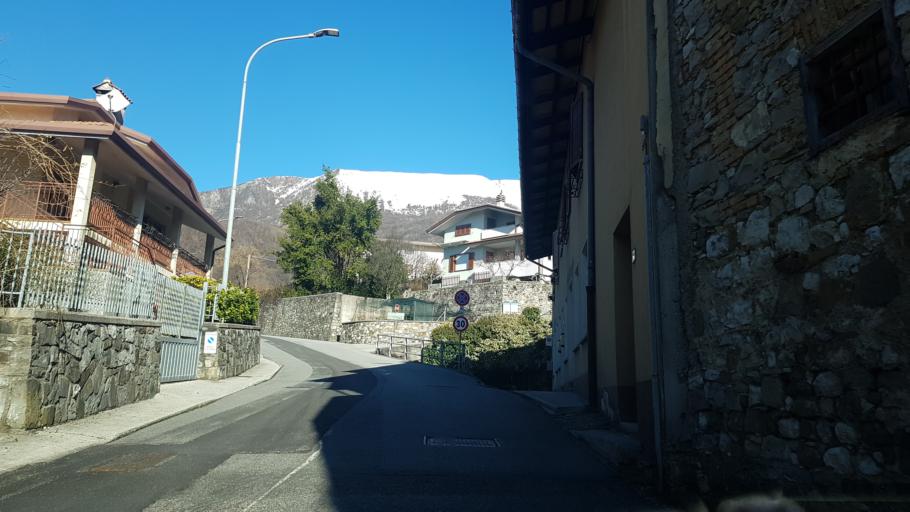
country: IT
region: Friuli Venezia Giulia
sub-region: Provincia di Udine
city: Montenars
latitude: 46.2535
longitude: 13.1681
